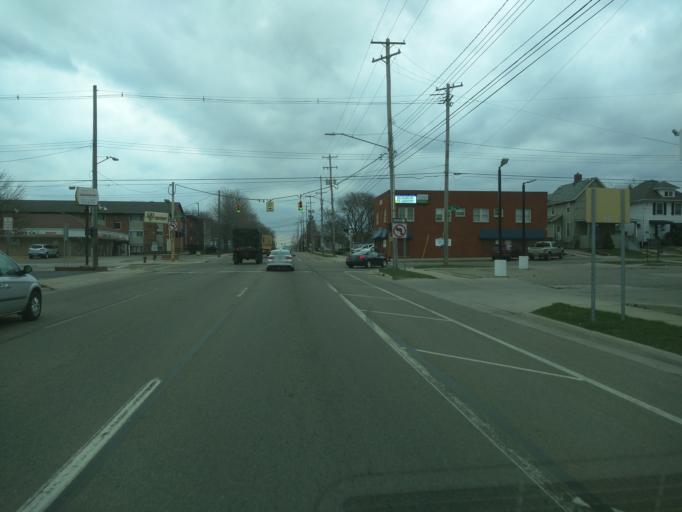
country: US
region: Michigan
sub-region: Ingham County
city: Lansing
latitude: 42.7409
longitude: -84.5605
